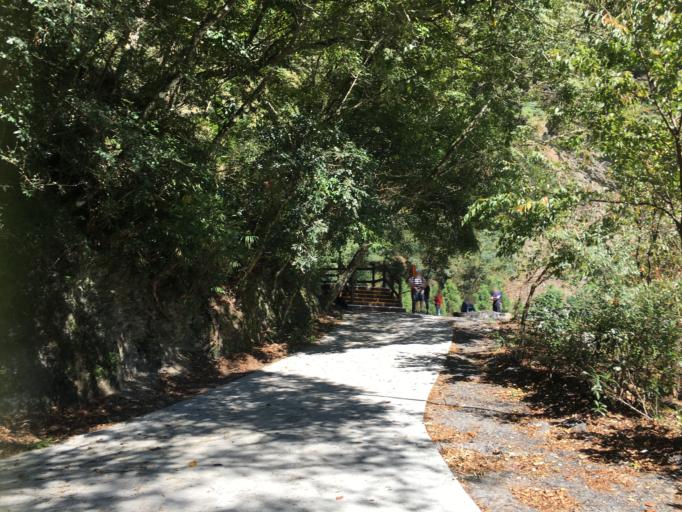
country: TW
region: Taiwan
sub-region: Nantou
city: Puli
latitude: 23.9521
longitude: 121.1824
